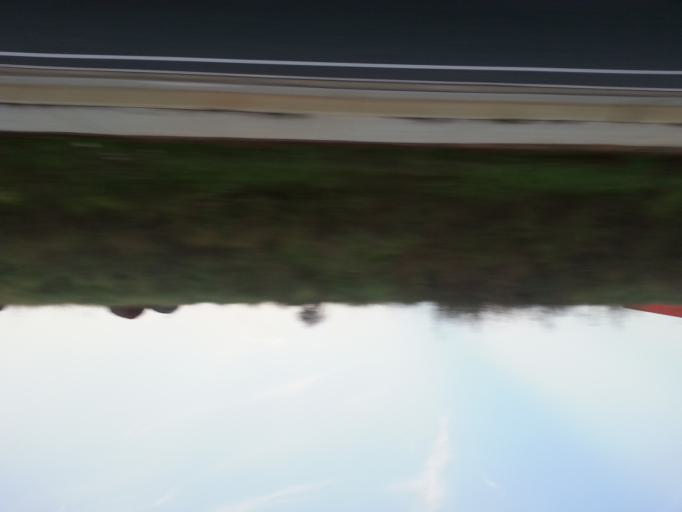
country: US
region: Tennessee
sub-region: Sevier County
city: Sevierville
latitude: 35.9344
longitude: -83.5830
